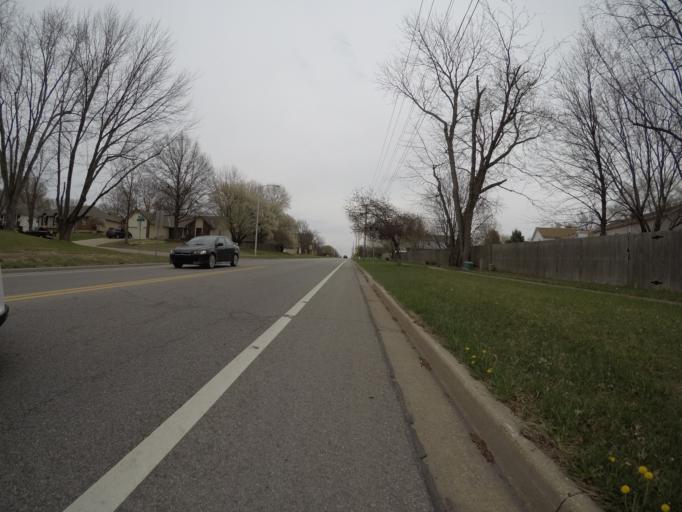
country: US
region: Kansas
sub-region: Johnson County
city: Olathe
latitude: 38.8690
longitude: -94.7740
